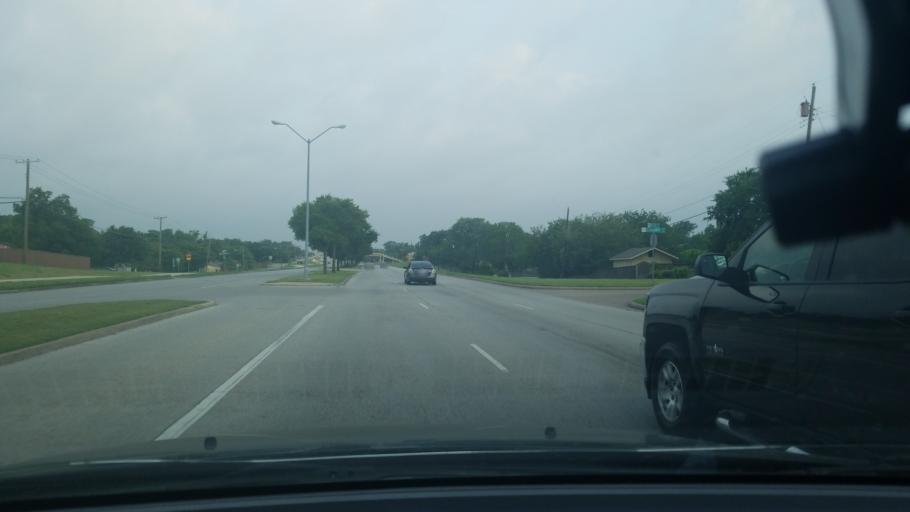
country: US
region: Texas
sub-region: Dallas County
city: Mesquite
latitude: 32.7681
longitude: -96.6312
